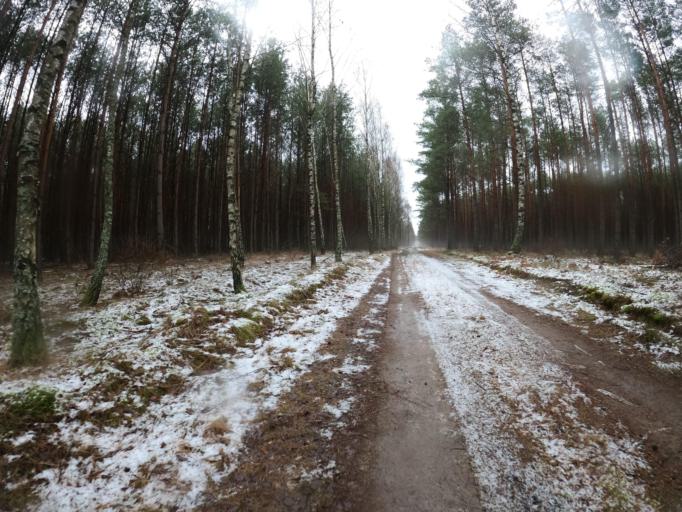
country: PL
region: Lubusz
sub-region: Powiat slubicki
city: Cybinka
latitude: 52.1996
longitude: 14.9228
